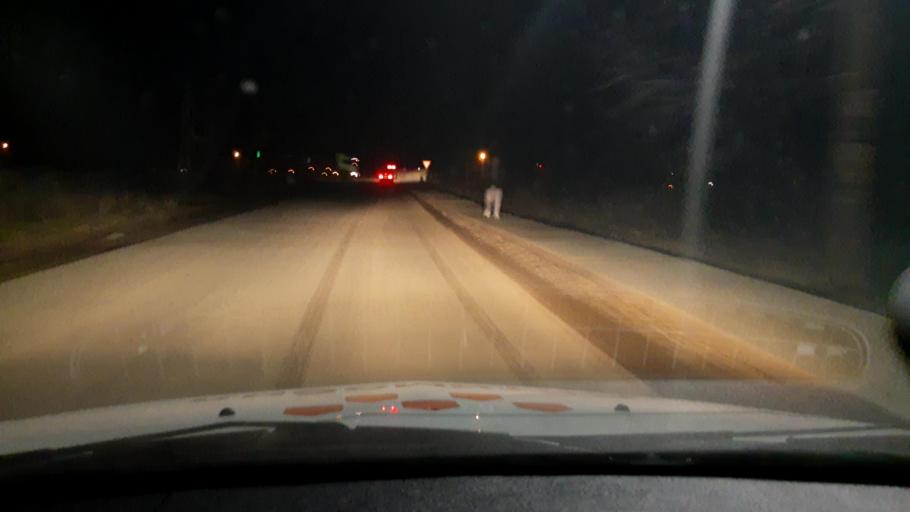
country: RU
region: Bashkortostan
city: Iglino
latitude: 54.7934
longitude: 56.2664
